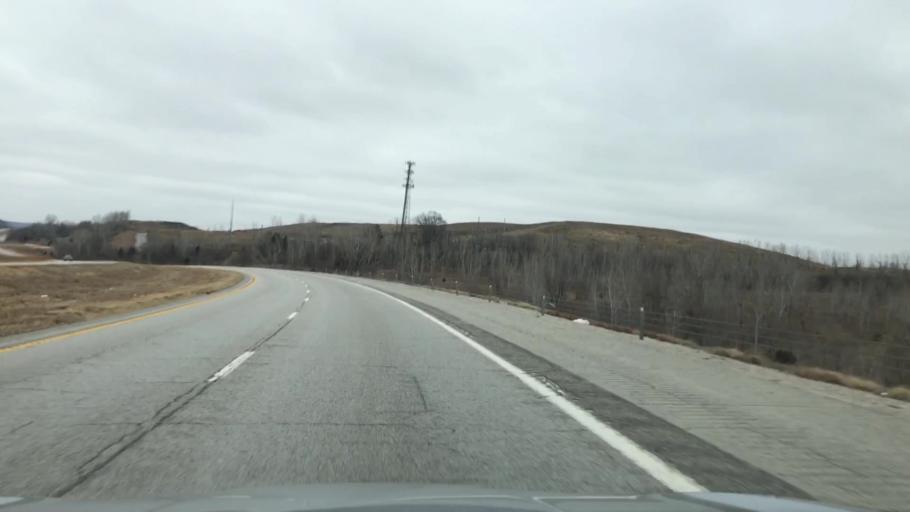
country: US
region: Missouri
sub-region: Jackson County
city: East Independence
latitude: 39.1320
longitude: -94.3836
